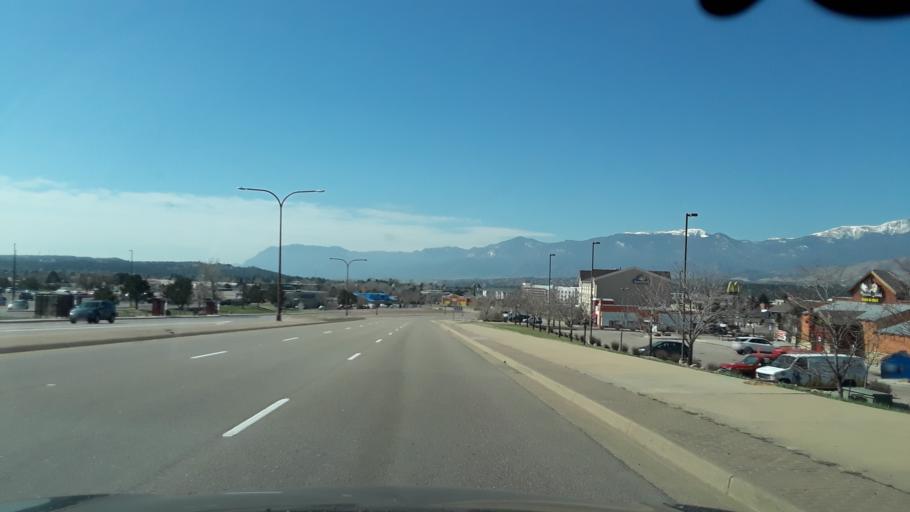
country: US
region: Colorado
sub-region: El Paso County
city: Air Force Academy
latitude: 38.9515
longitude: -104.8013
